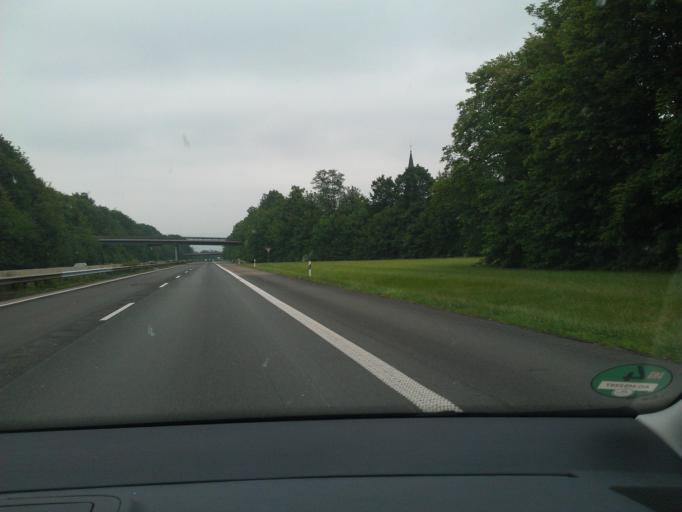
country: DE
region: Rheinland-Pfalz
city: Mulheim-Karlich
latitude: 50.3728
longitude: 7.5123
